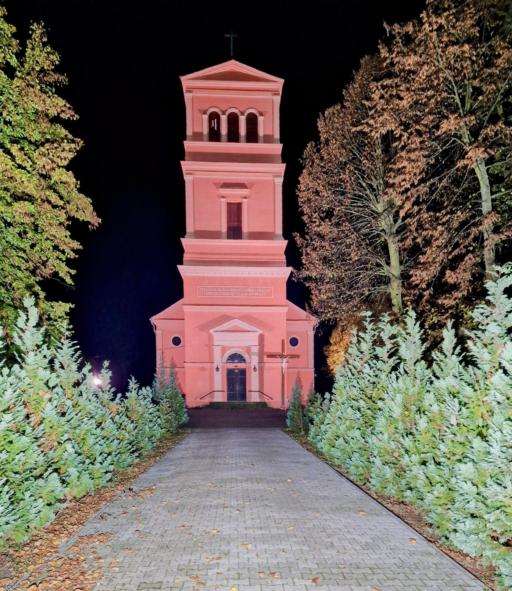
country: PL
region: Lubusz
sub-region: Powiat zielonogorski
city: Trzebiechow
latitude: 52.0199
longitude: 15.7338
